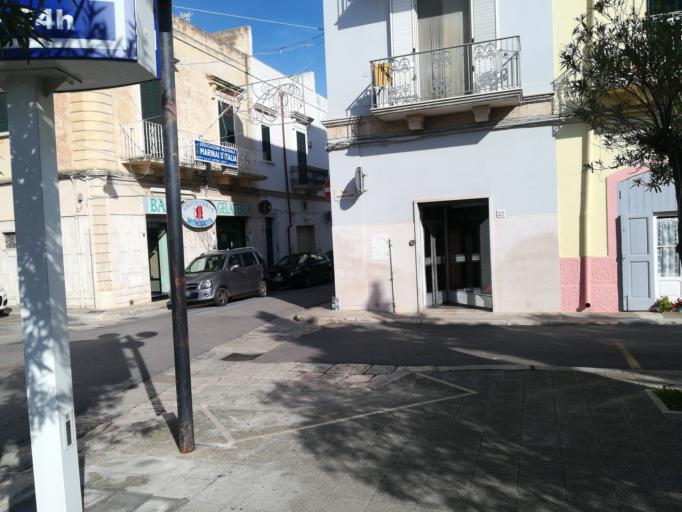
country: IT
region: Apulia
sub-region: Provincia di Bari
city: Polignano a Mare
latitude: 40.9933
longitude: 17.2197
